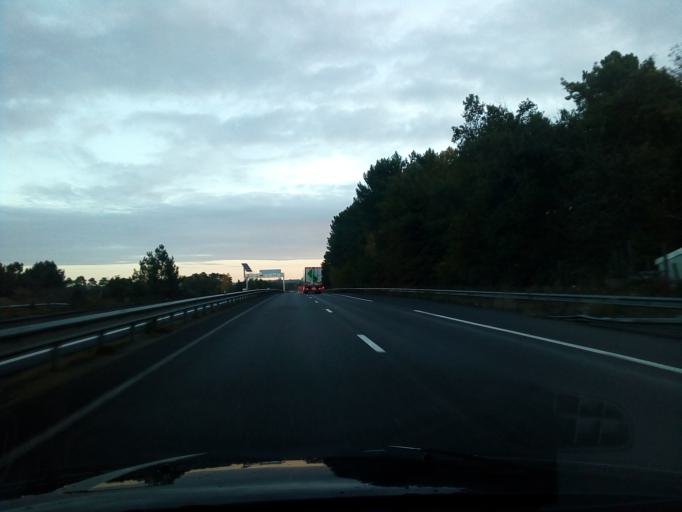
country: FR
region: Aquitaine
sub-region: Departement de la Gironde
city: Laruscade
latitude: 45.1914
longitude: -0.3130
